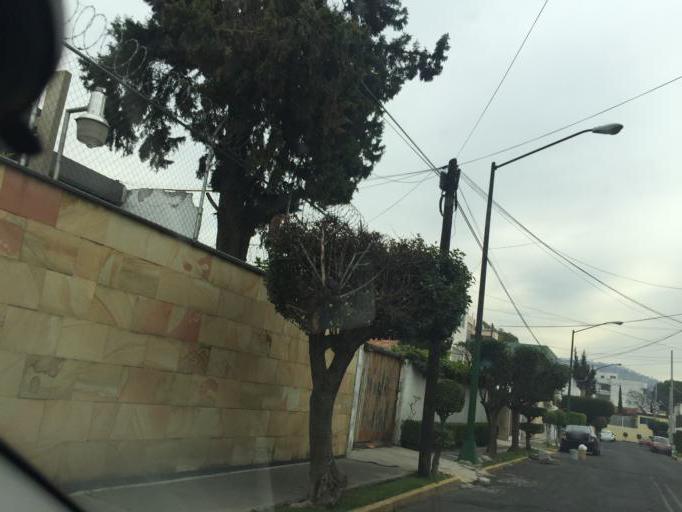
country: MX
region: Mexico
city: Colonia Lindavista
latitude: 19.4905
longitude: -99.1288
